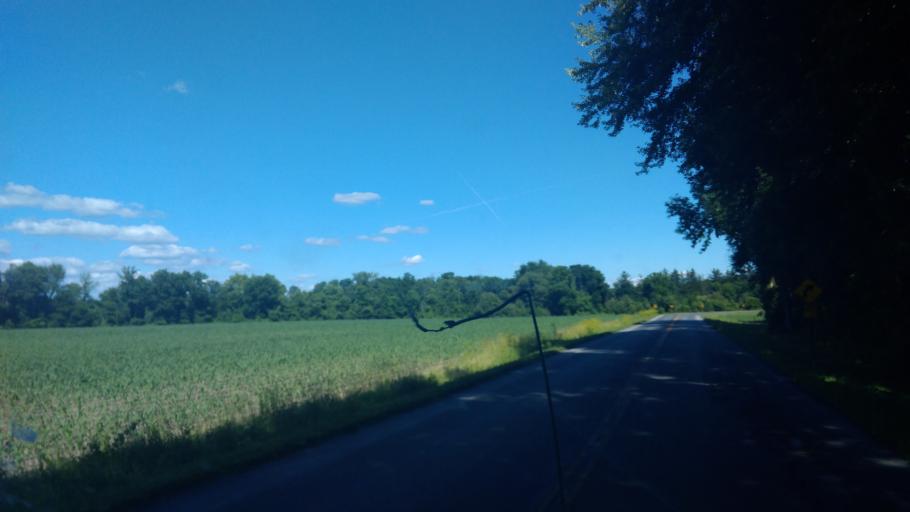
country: US
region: New York
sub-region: Wayne County
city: Lyons
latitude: 43.0259
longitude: -76.9474
